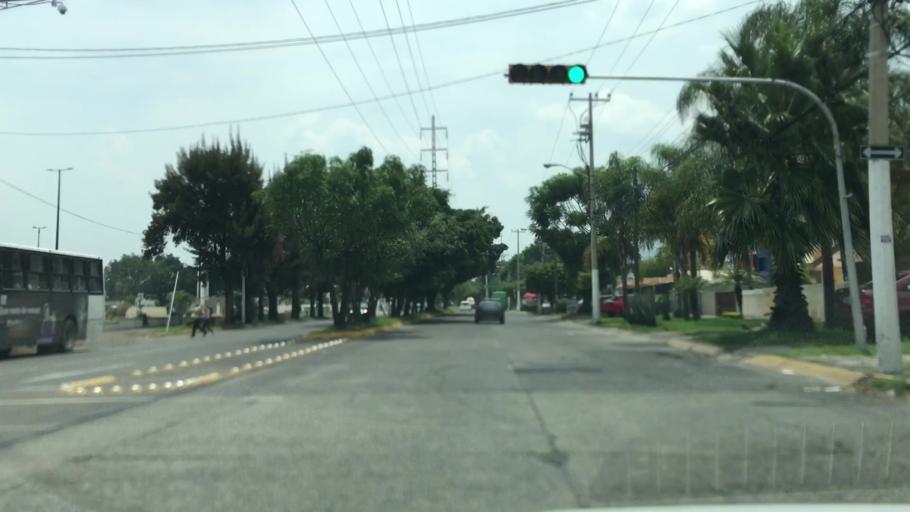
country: MX
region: Jalisco
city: Guadalajara
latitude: 20.6502
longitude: -103.4203
